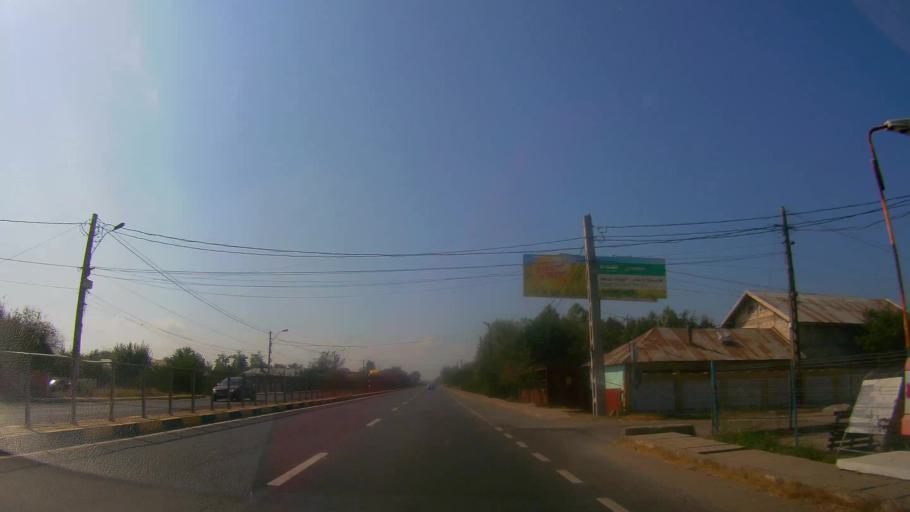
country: RO
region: Giurgiu
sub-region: Comuna Fratesti
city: Remus
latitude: 43.9487
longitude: 25.9803
